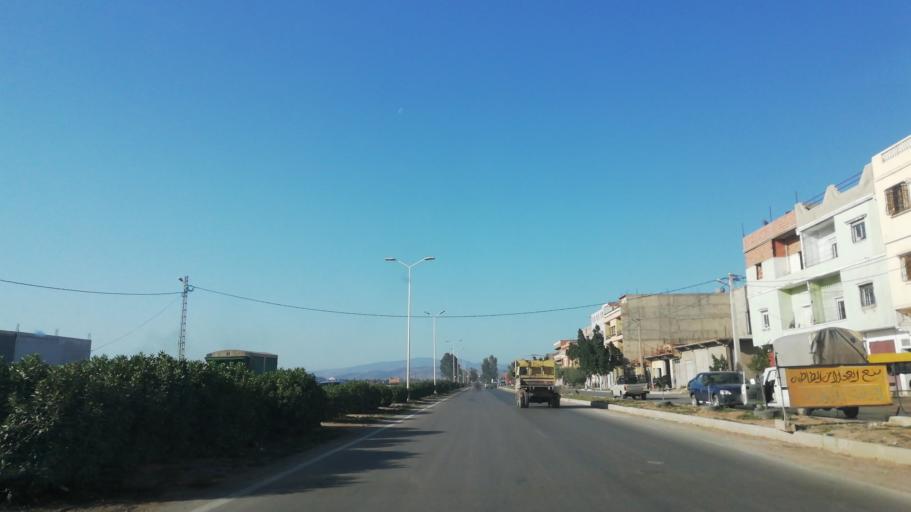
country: DZ
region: Mascara
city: Mascara
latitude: 35.6131
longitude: 0.1021
